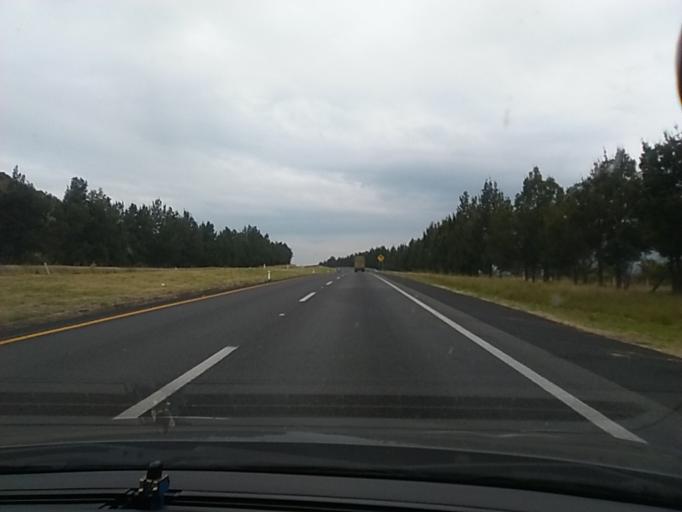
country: MX
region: Michoacan
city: Churintzio
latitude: 20.0998
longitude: -102.0277
